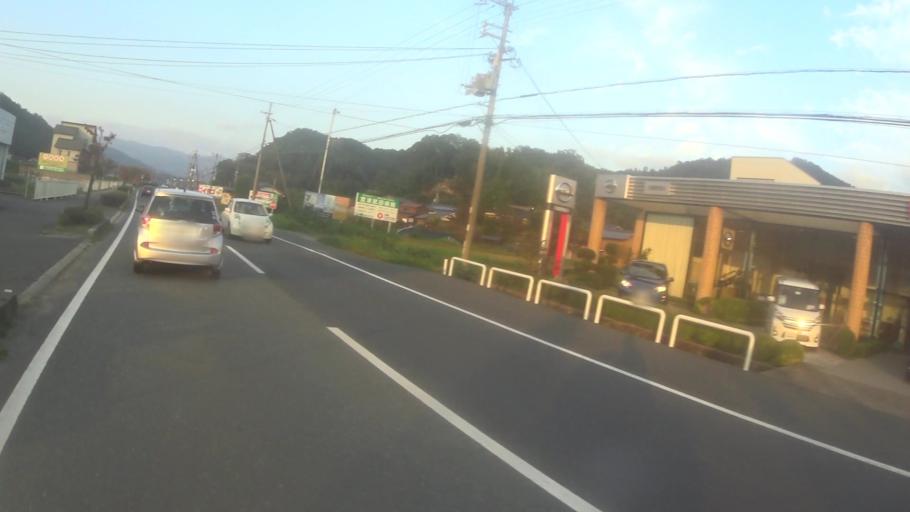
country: JP
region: Kyoto
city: Miyazu
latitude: 35.5430
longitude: 135.1328
